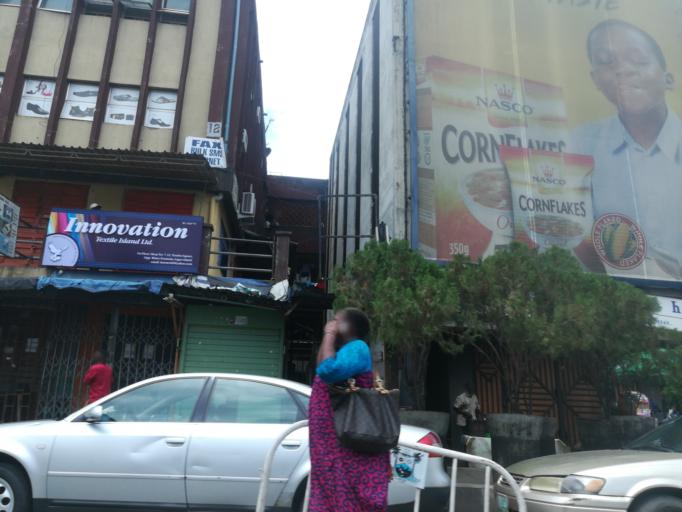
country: NG
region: Lagos
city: Lagos
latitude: 6.4539
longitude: 3.3898
